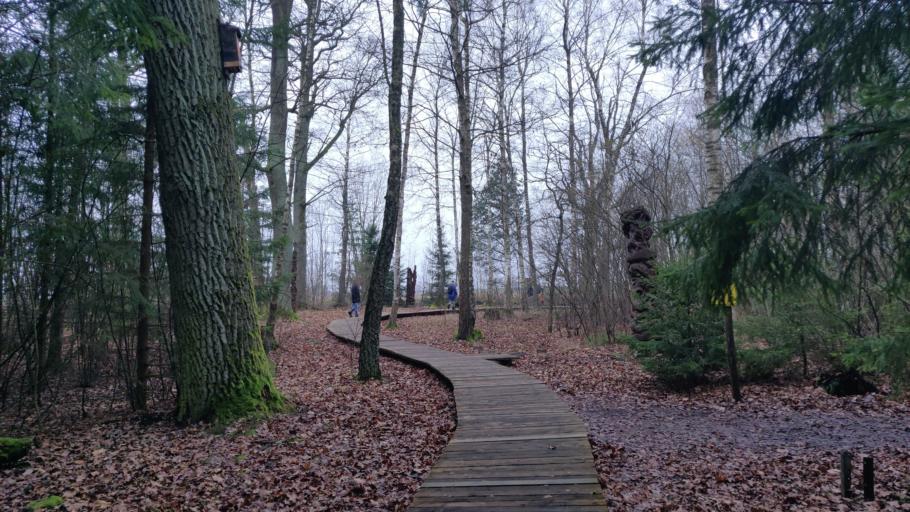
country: LT
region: Vilnius County
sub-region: Vilniaus Rajonas
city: Vievis
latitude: 54.8346
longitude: 24.9506
